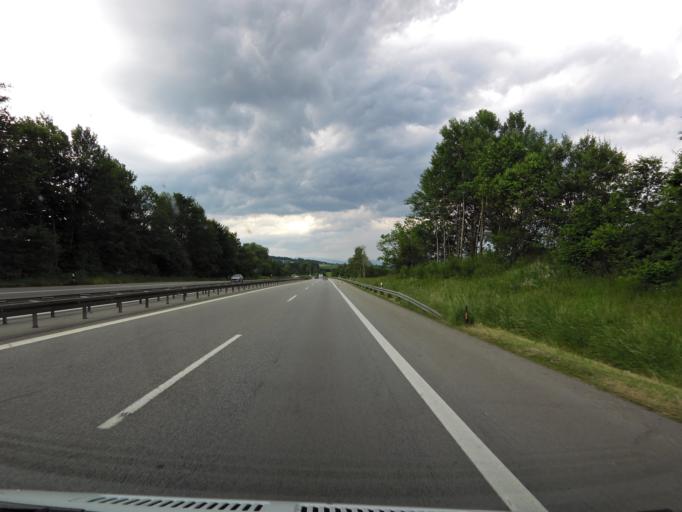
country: DE
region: Bavaria
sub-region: Lower Bavaria
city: Aussernzell
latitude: 48.6968
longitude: 13.1930
